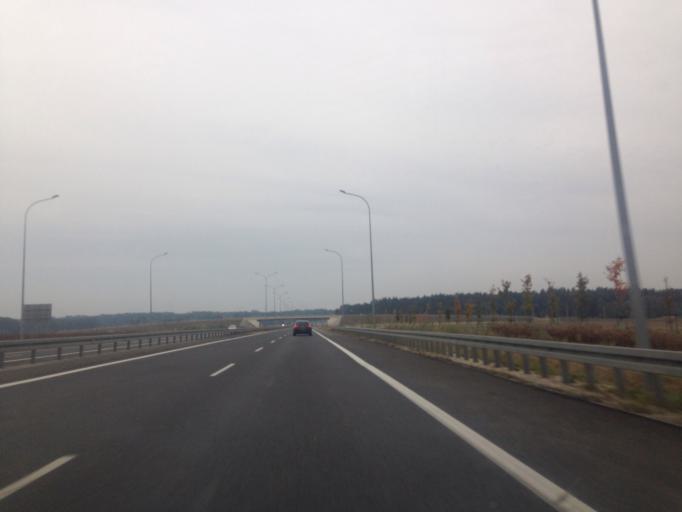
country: PL
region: Greater Poland Voivodeship
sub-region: Powiat poznanski
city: Pobiedziska
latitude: 52.4161
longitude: 17.2918
